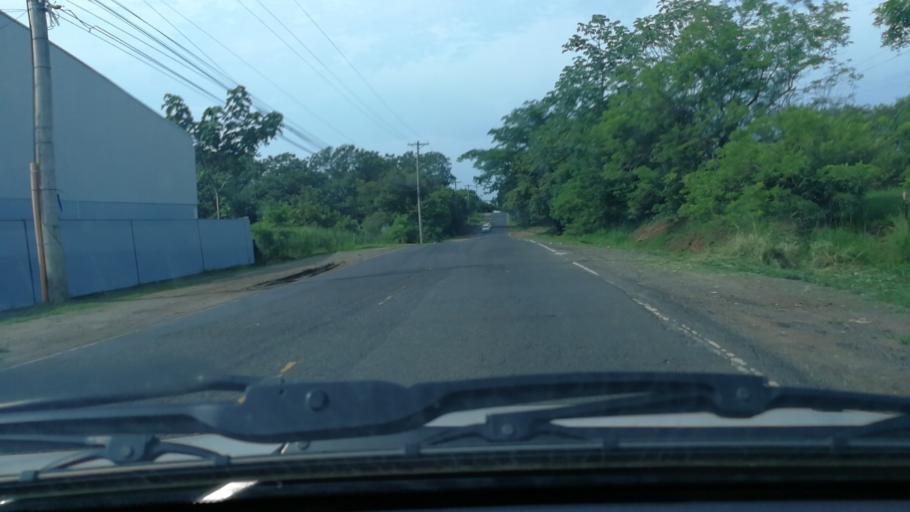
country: PA
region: Panama
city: Pacora
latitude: 9.0947
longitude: -79.2885
